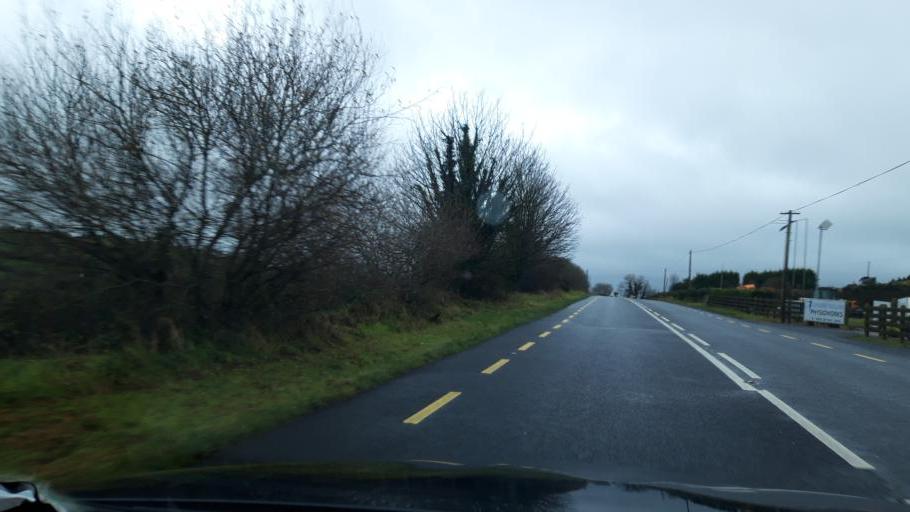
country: IE
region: Ulster
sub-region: County Monaghan
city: Castleblayney
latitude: 54.0877
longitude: -6.6910
